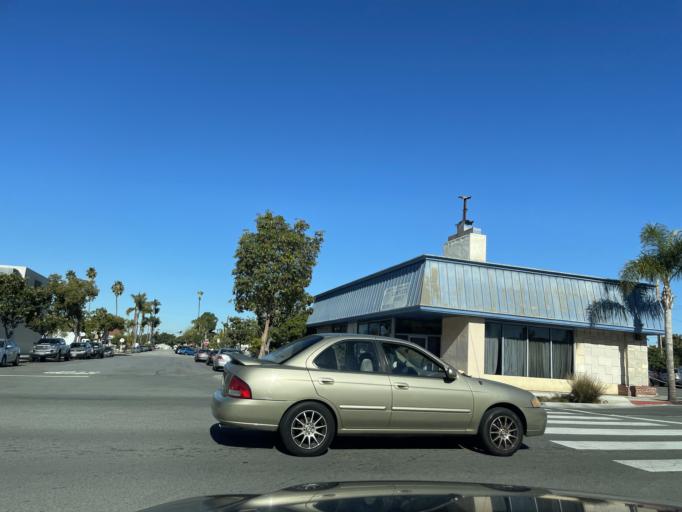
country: US
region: California
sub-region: San Diego County
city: National City
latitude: 32.6766
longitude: -117.1038
